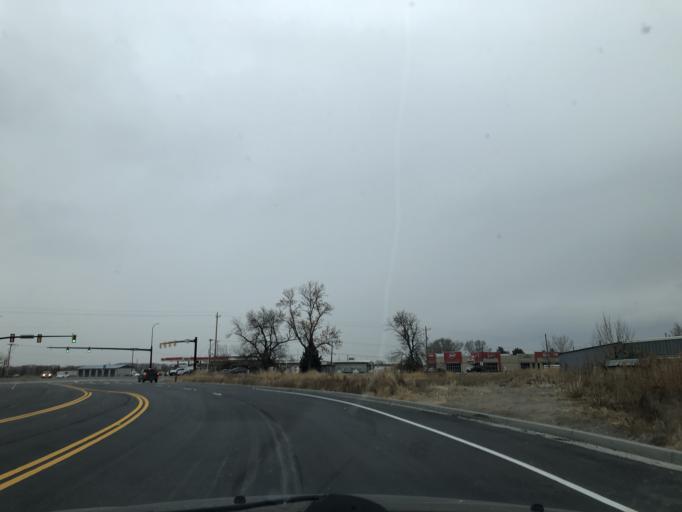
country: US
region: Utah
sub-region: Cache County
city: Nibley
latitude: 41.6963
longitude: -111.8587
